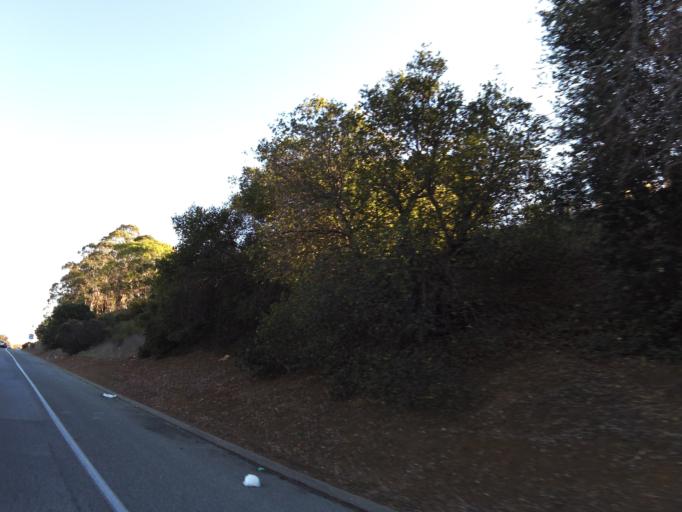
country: US
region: California
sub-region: Santa Clara County
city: Loyola
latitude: 37.3387
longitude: -122.0863
